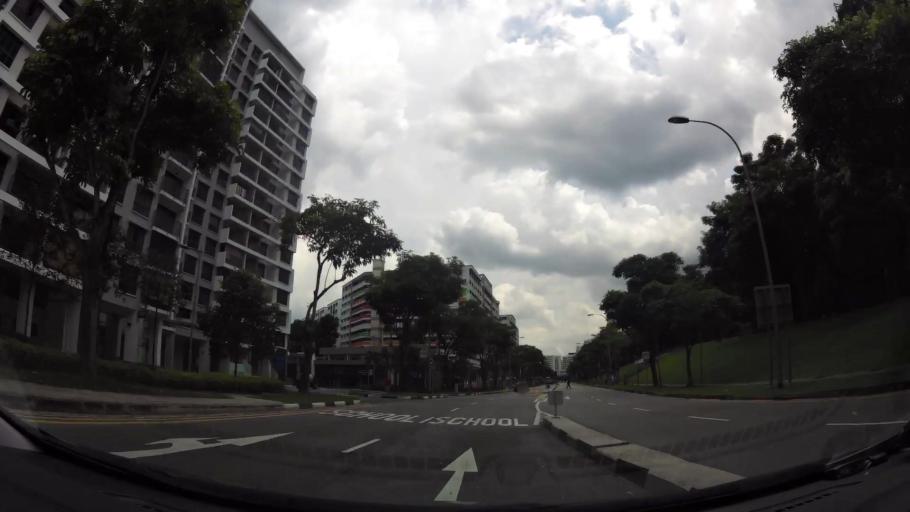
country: MY
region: Johor
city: Kampung Pasir Gudang Baru
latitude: 1.4269
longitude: 103.8422
